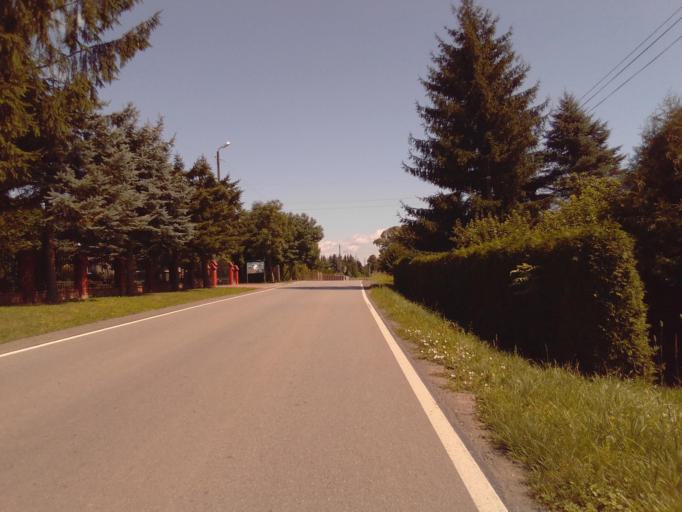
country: PL
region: Subcarpathian Voivodeship
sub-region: Powiat krosnienski
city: Jedlicze
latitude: 49.6977
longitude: 21.6184
